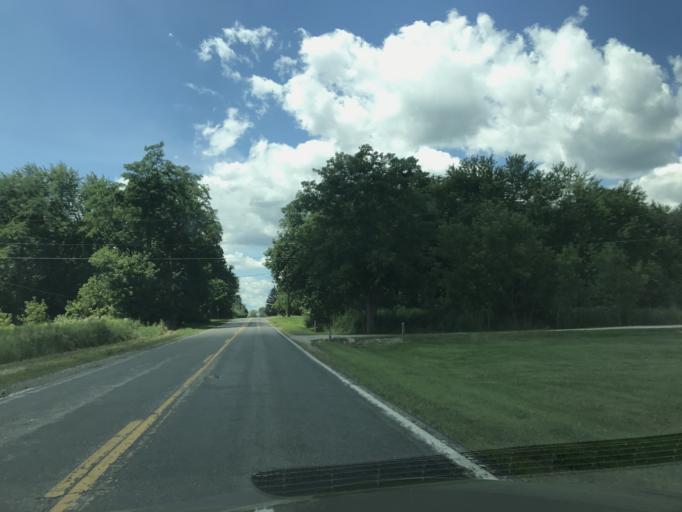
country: US
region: Michigan
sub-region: Ingham County
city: Leslie
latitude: 42.4510
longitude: -84.5002
